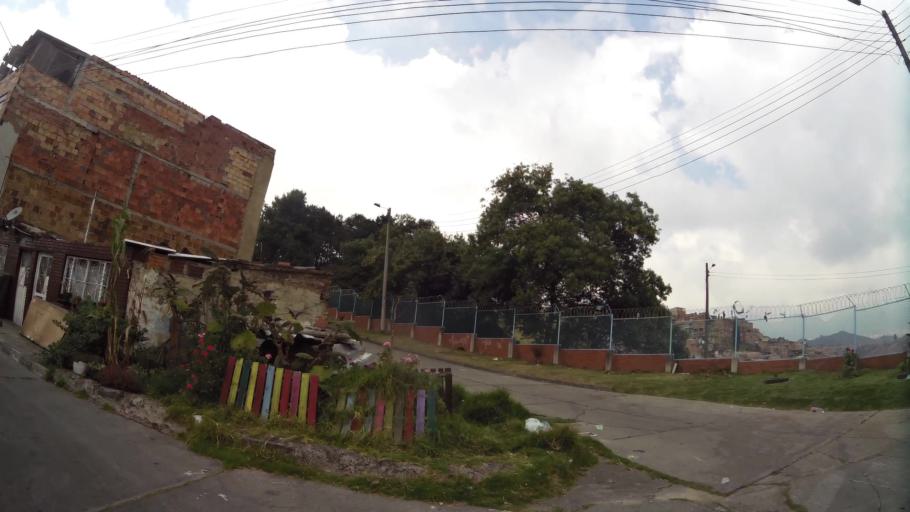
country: CO
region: Bogota D.C.
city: Bogota
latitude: 4.5737
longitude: -74.1198
